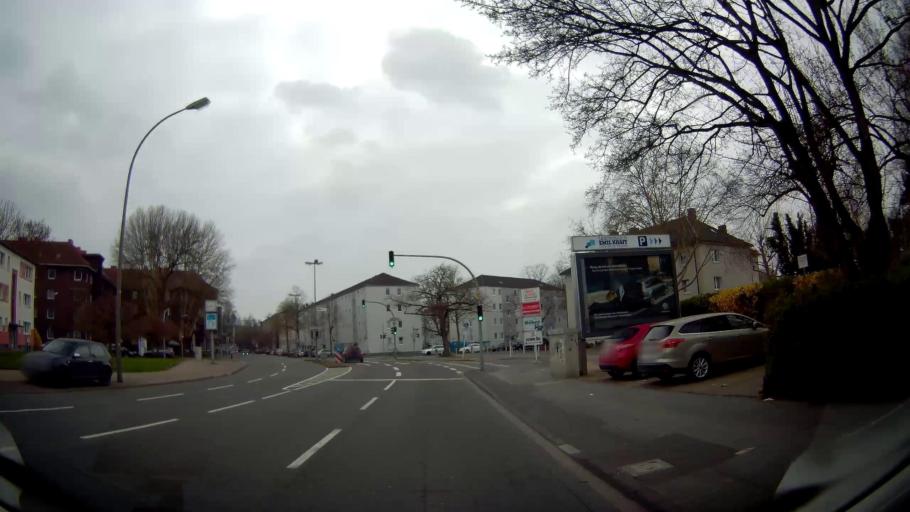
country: DE
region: North Rhine-Westphalia
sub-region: Regierungsbezirk Arnsberg
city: Dortmund
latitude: 51.5187
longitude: 7.4878
